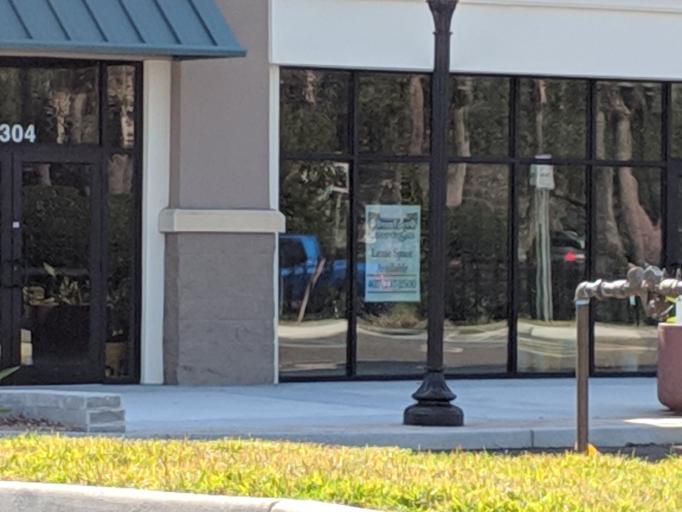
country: US
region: Florida
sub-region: Polk County
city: Loughman
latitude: 28.2617
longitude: -81.6184
